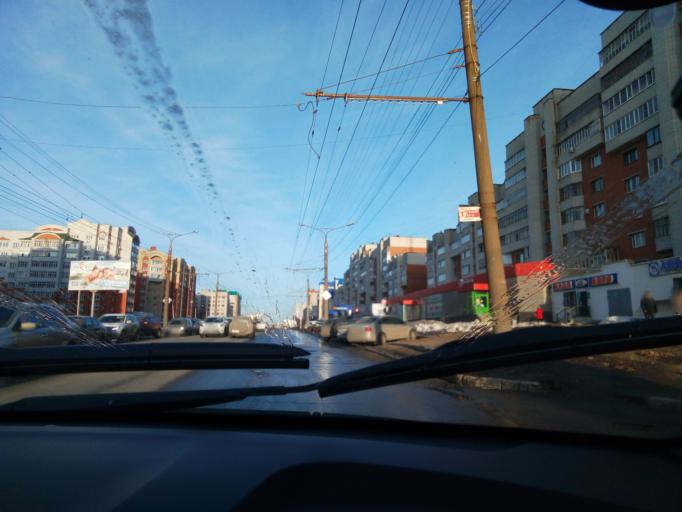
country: RU
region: Chuvashia
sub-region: Cheboksarskiy Rayon
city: Cheboksary
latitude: 56.1487
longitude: 47.1730
